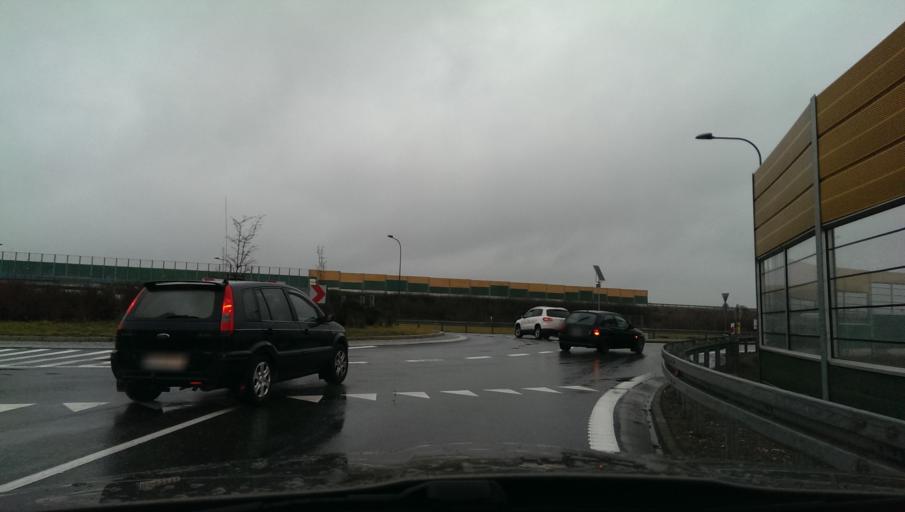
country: PL
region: Subcarpathian Voivodeship
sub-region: Powiat rzeszowski
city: Rudna Mala
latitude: 50.1063
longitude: 21.9762
